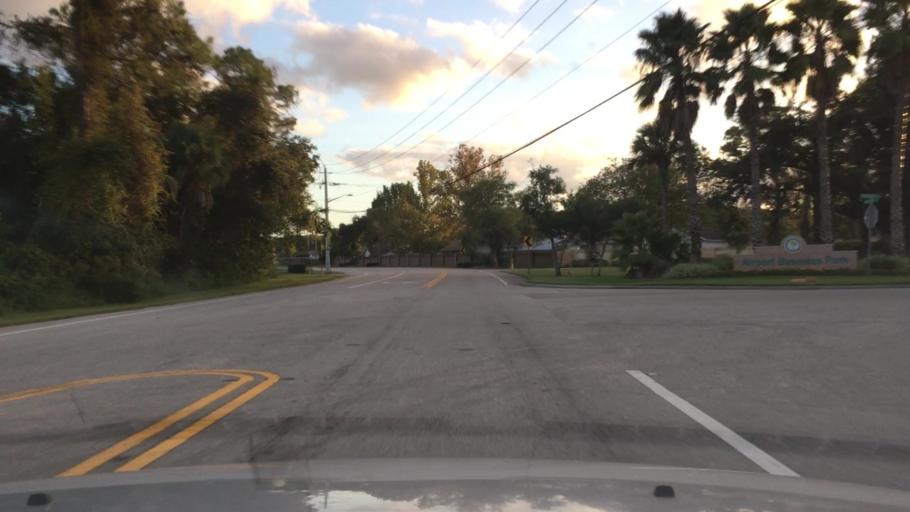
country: US
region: Florida
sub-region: Volusia County
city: Ormond Beach
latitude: 29.2896
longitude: -81.1130
